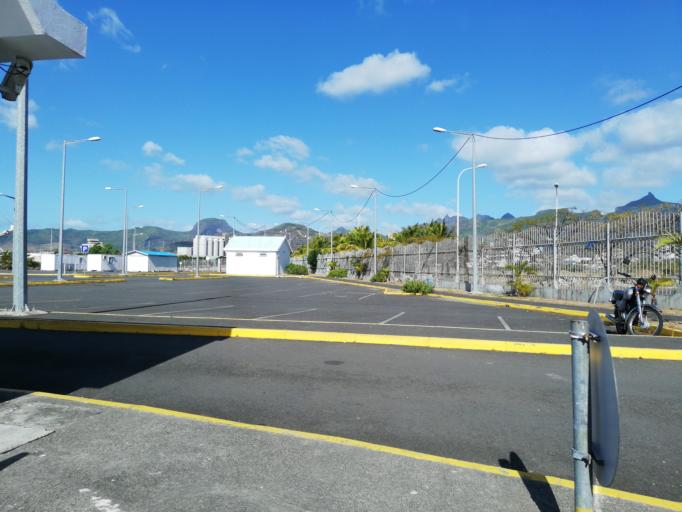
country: MU
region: Port Louis
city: Port Louis
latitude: -20.1565
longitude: 57.4914
